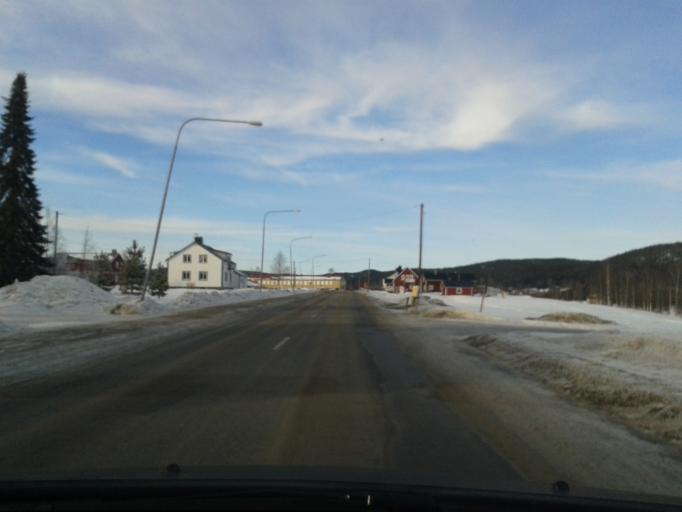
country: SE
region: Vaesternorrland
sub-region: OErnskoeldsviks Kommun
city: Bredbyn
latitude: 63.5102
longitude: 18.0669
